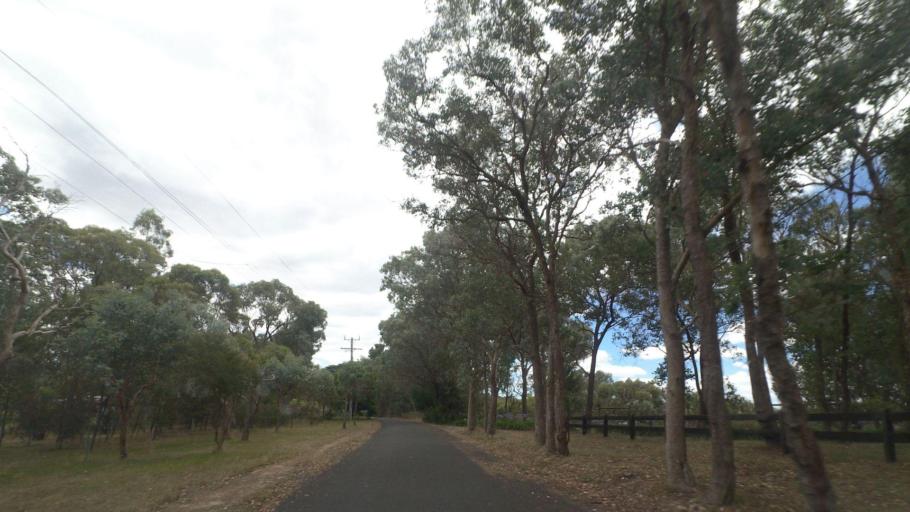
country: AU
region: Victoria
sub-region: Manningham
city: Warrandyte
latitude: -37.7503
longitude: 145.2517
